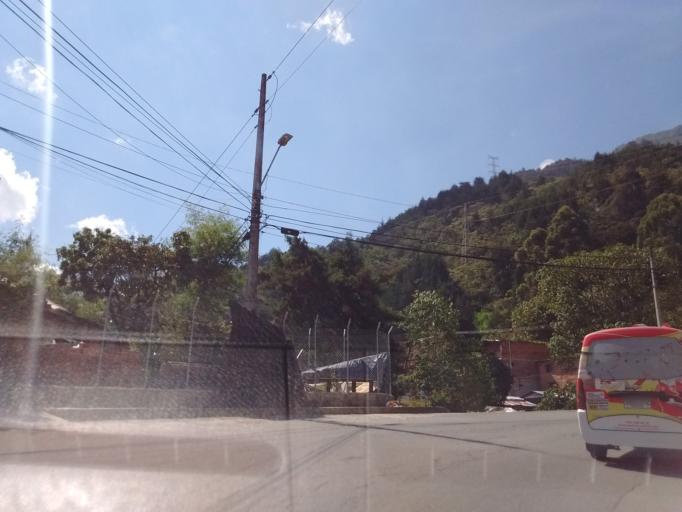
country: CO
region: Antioquia
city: Medellin
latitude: 6.2281
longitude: -75.5324
